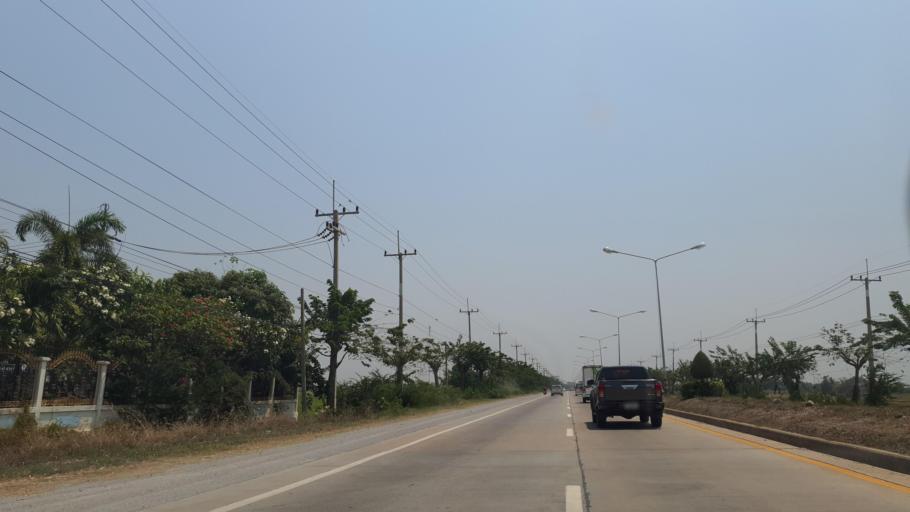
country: TH
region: Suphan Buri
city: U Thong
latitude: 14.4187
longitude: 99.9750
